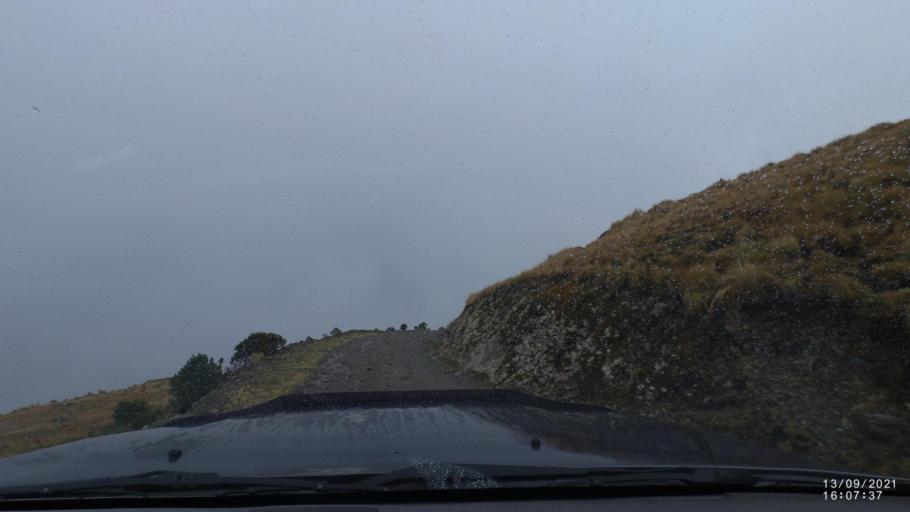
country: BO
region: Cochabamba
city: Colomi
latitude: -17.2791
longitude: -65.7086
